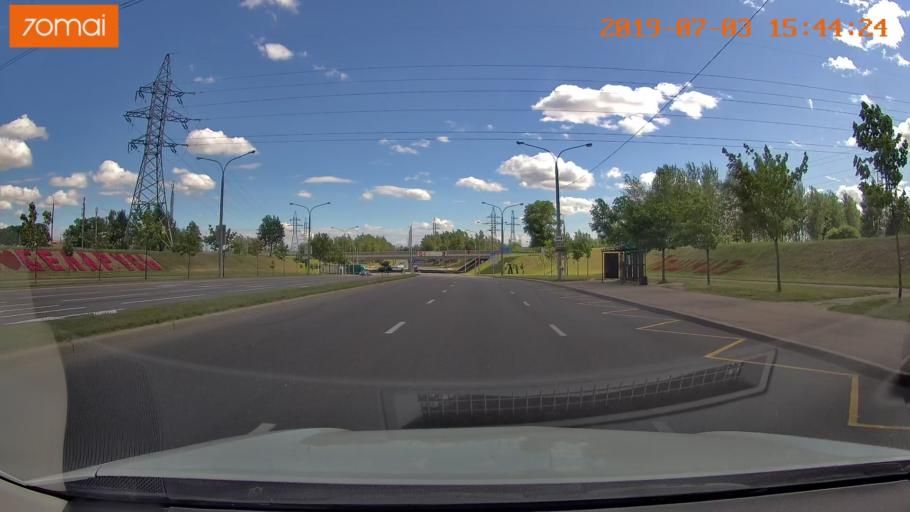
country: BY
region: Minsk
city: Syenitsa
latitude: 53.8351
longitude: 27.5745
